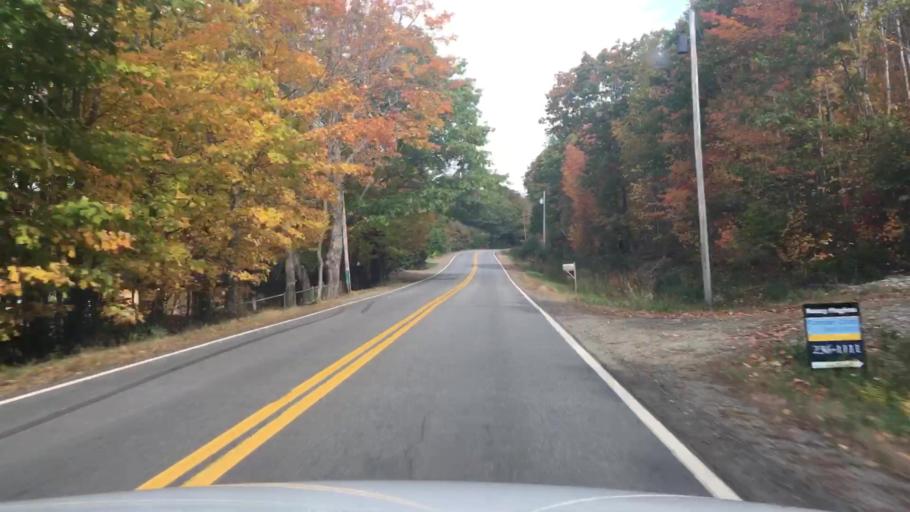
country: US
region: Maine
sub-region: Waldo County
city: Searsmont
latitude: 44.3328
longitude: -69.1389
